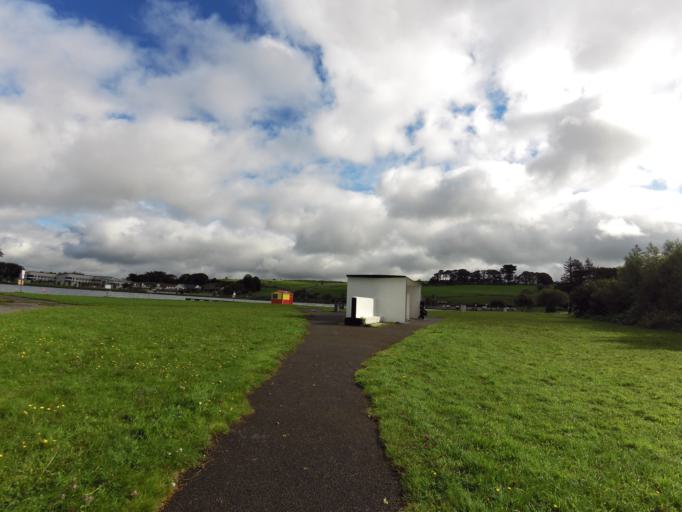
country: IE
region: Connaught
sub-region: County Galway
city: Loughrea
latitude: 53.1854
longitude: -8.5634
